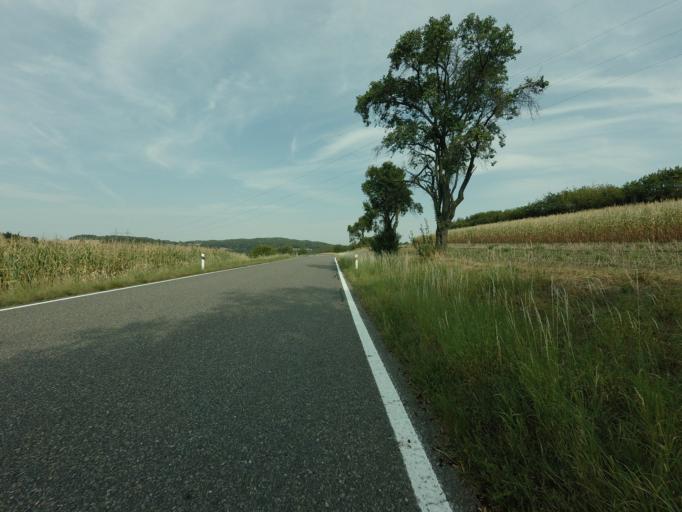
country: CZ
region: Central Bohemia
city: Petrovice
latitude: 49.5185
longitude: 14.3573
